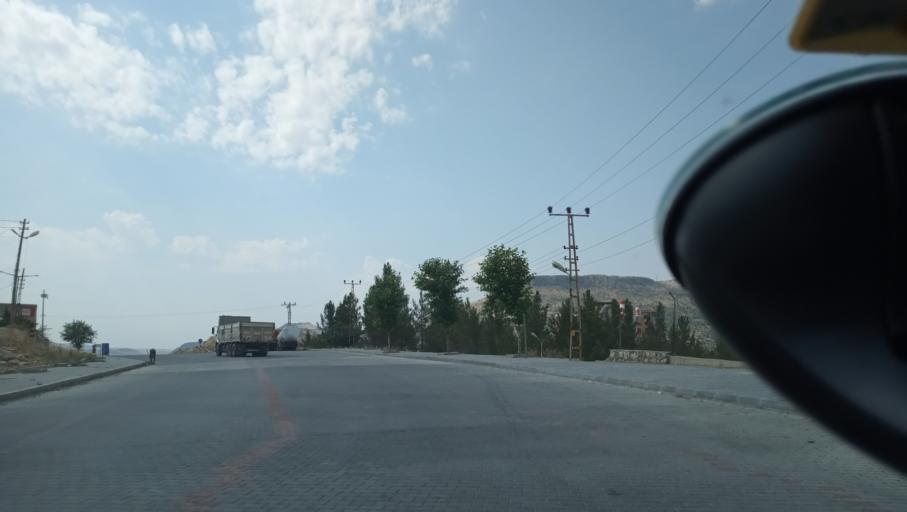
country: TR
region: Mardin
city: Kabala
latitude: 37.3441
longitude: 40.8040
